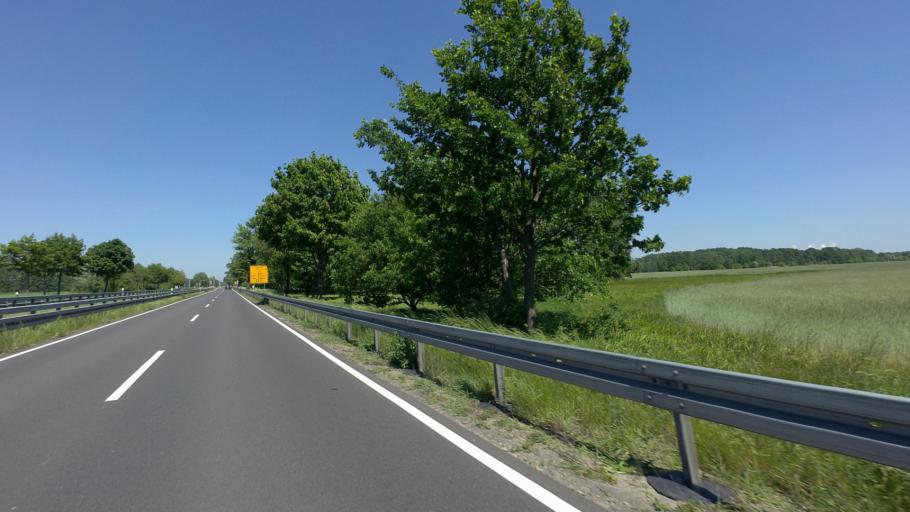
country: DE
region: Brandenburg
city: Peitz
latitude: 51.8229
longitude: 14.3866
